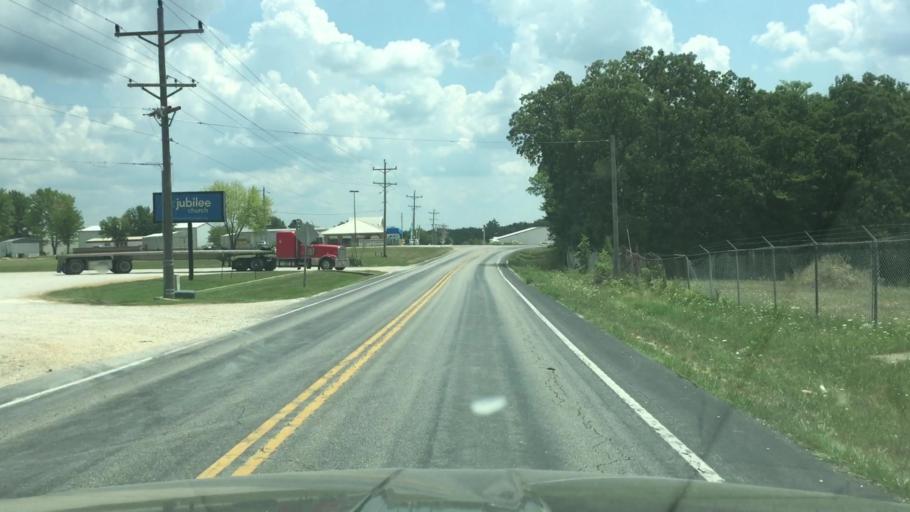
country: US
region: Missouri
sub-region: Camden County
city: Osage Beach
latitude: 38.1396
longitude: -92.5834
